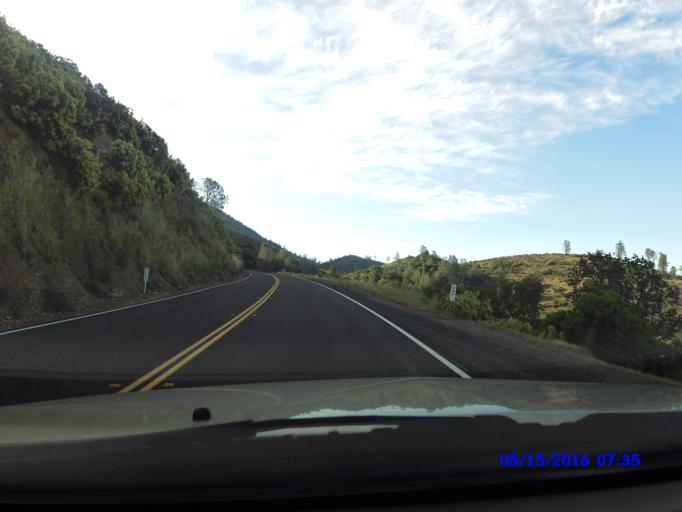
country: US
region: California
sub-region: Mariposa County
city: Mariposa
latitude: 37.6798
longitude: -120.1711
